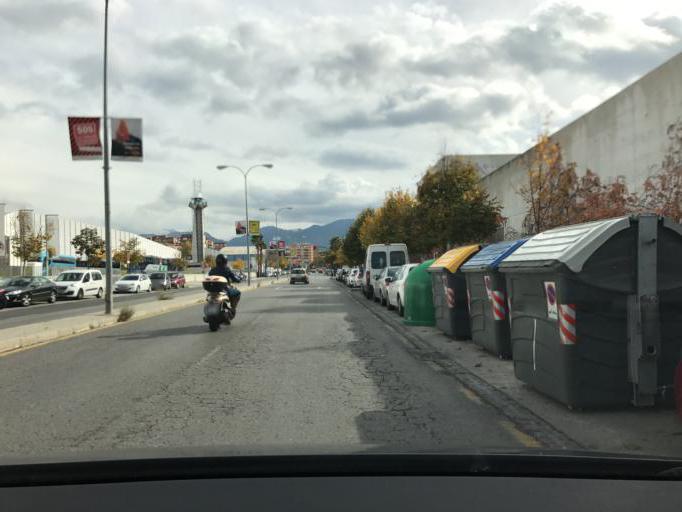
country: ES
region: Andalusia
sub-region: Provincia de Granada
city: Armilla
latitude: 37.1627
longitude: -3.6078
